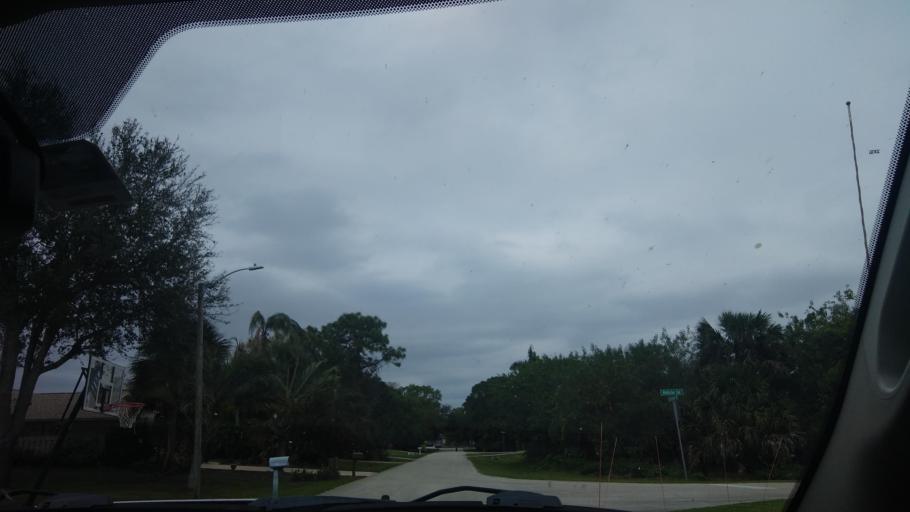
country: US
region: Florida
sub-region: Indian River County
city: Sebastian
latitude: 27.7706
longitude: -80.4936
